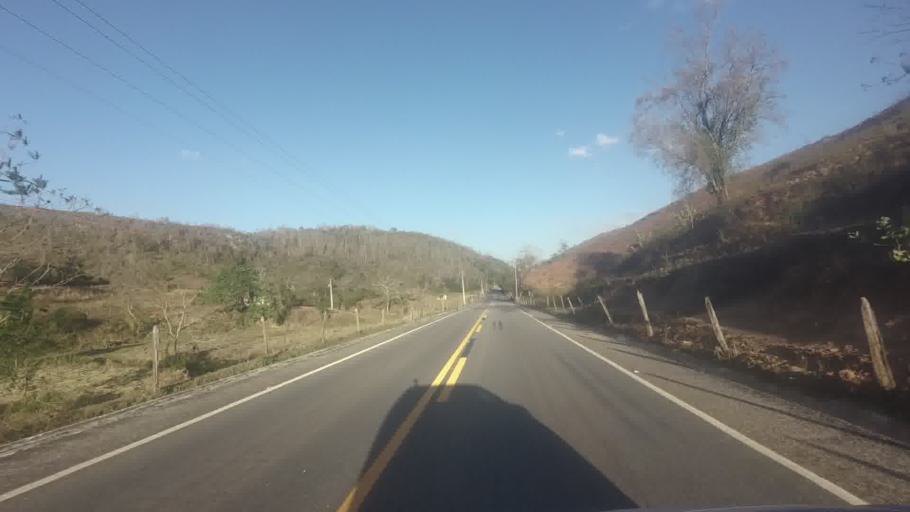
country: BR
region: Espirito Santo
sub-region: Cachoeiro De Itapemirim
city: Cachoeiro de Itapemirim
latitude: -20.8230
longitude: -41.2001
